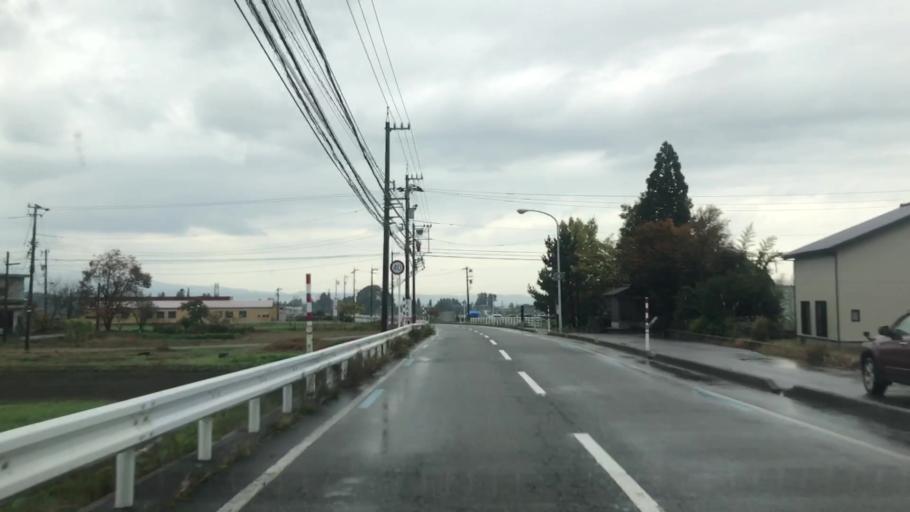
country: JP
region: Toyama
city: Toyama-shi
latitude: 36.6078
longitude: 137.2772
